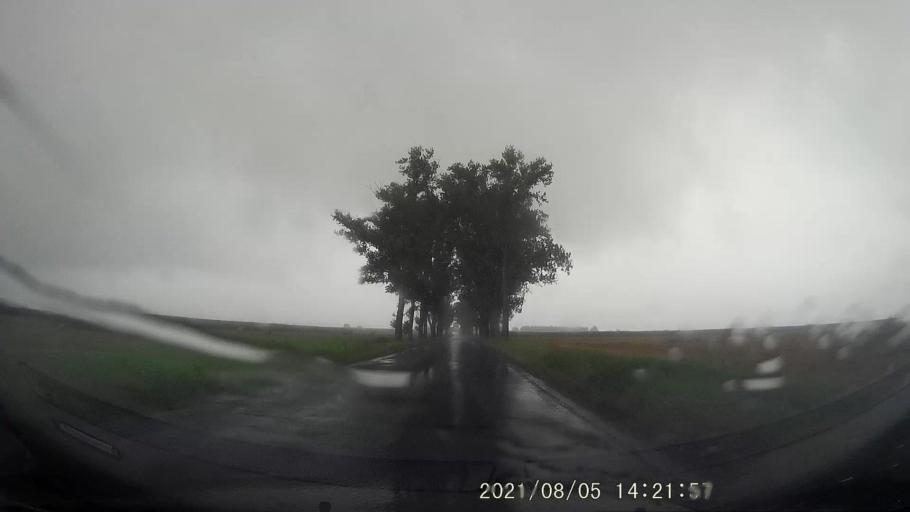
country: PL
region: Opole Voivodeship
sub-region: Powiat nyski
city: Korfantow
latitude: 50.4732
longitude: 17.6644
